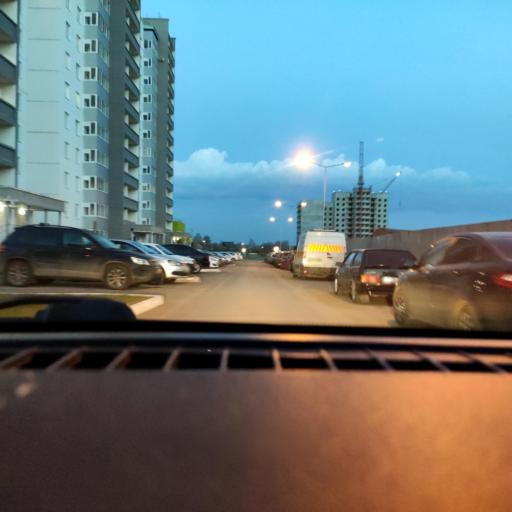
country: RU
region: Perm
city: Perm
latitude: 58.0534
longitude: 56.3485
